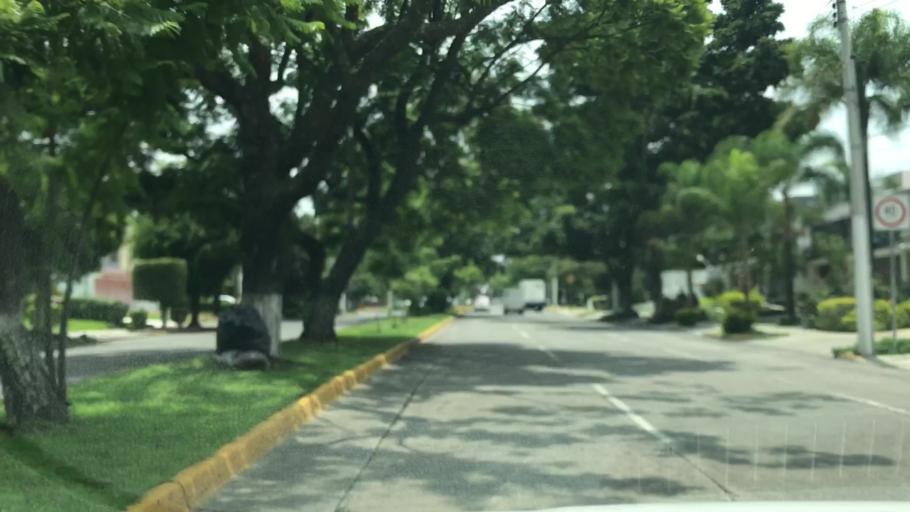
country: MX
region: Jalisco
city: Guadalajara
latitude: 20.6508
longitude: -103.4111
